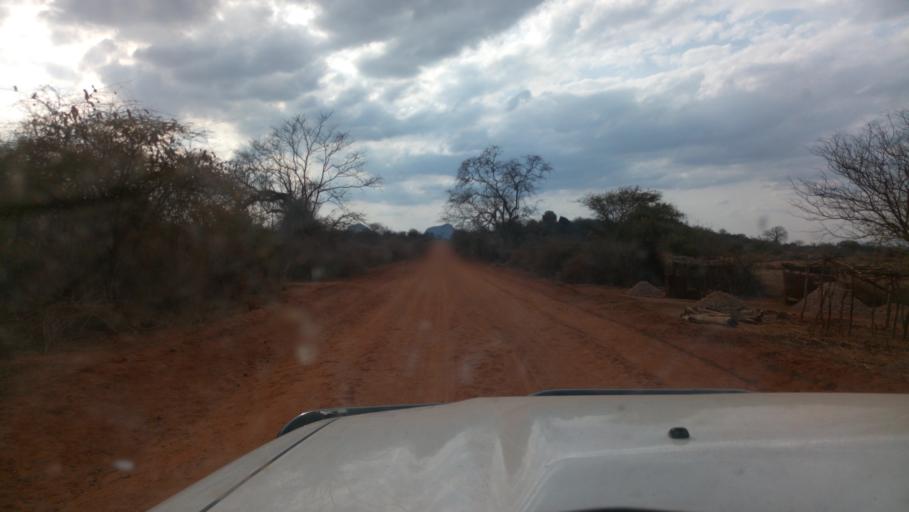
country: KE
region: Kitui
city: Kitui
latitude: -1.7400
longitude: 38.4035
